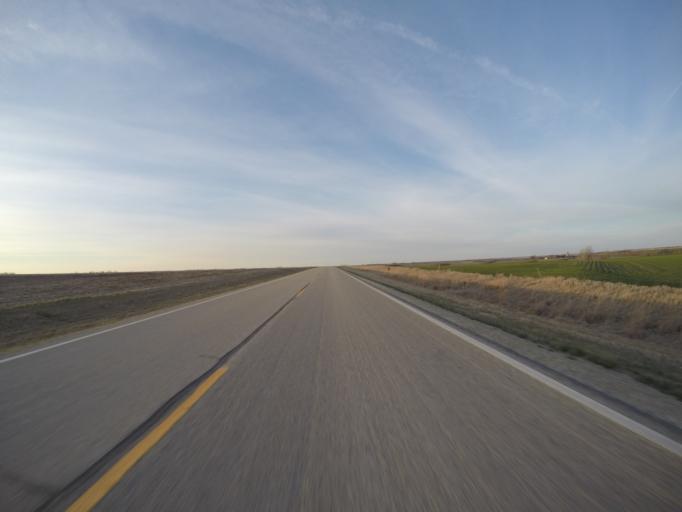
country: US
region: Kansas
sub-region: Riley County
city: Fort Riley North
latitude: 39.3721
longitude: -96.8496
